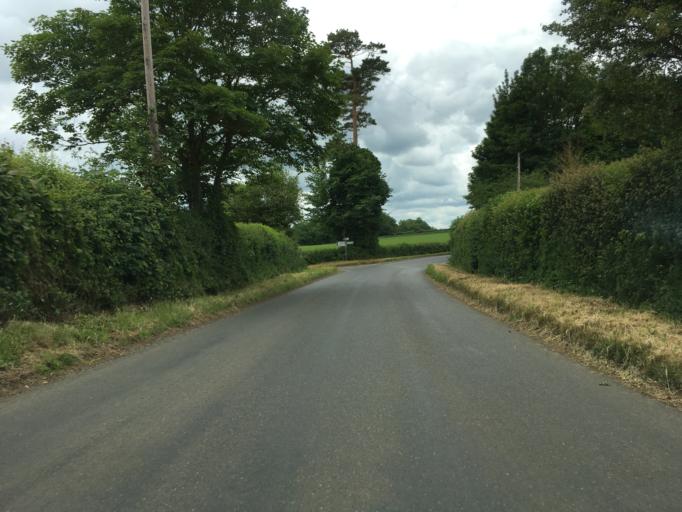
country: GB
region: England
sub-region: Wiltshire
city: Norton
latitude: 51.5232
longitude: -2.1675
